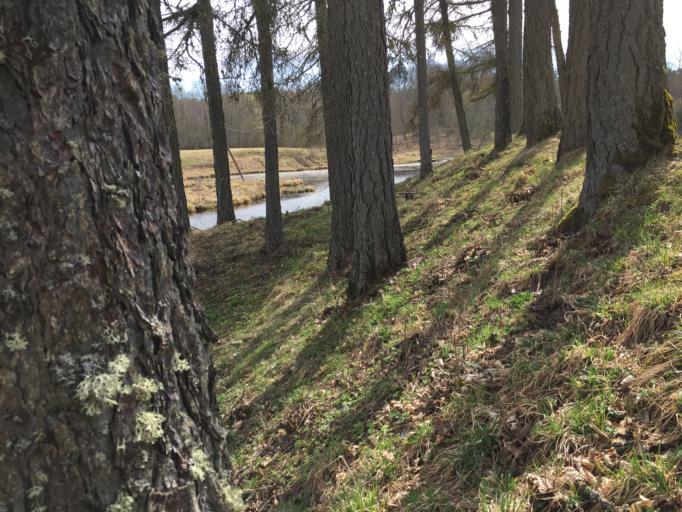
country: LV
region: Strenci
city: Seda
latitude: 57.8094
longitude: 25.8319
